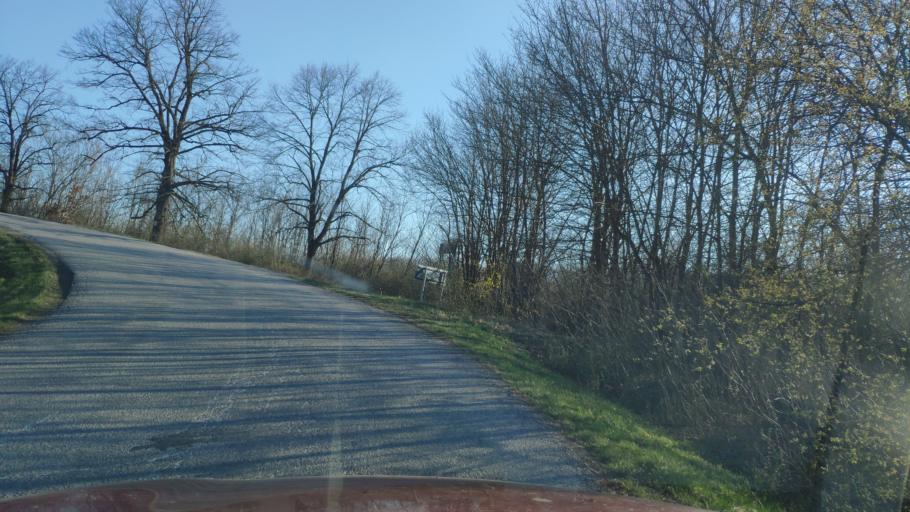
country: SK
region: Banskobystricky
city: Revuca
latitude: 48.5002
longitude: 20.2547
